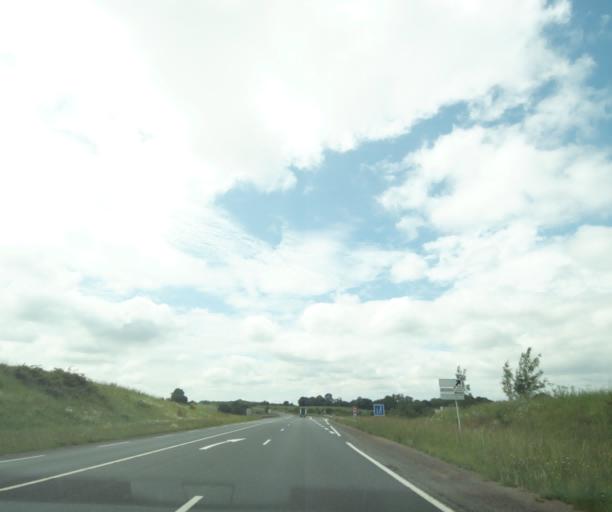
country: FR
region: Poitou-Charentes
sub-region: Departement des Deux-Sevres
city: Saint-Pardoux
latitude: 46.5271
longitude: -0.3218
